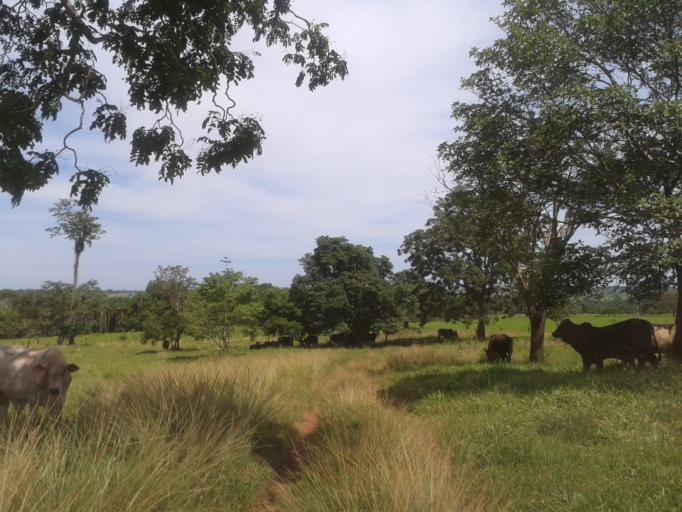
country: BR
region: Minas Gerais
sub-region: Santa Vitoria
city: Santa Vitoria
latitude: -19.1276
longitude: -50.5523
